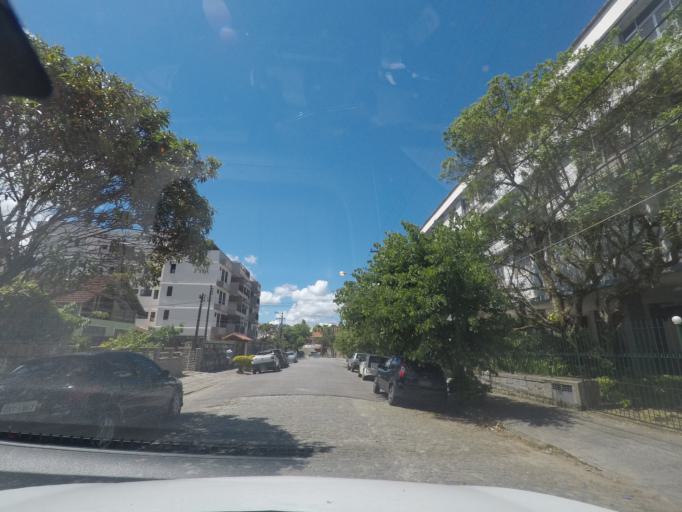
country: BR
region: Rio de Janeiro
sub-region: Teresopolis
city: Teresopolis
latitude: -22.4338
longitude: -42.9774
